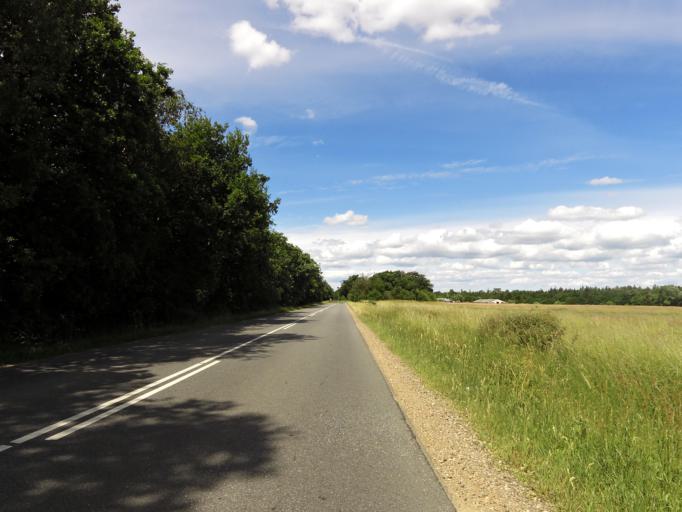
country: DK
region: South Denmark
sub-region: Esbjerg Kommune
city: Ribe
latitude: 55.2950
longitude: 8.7733
